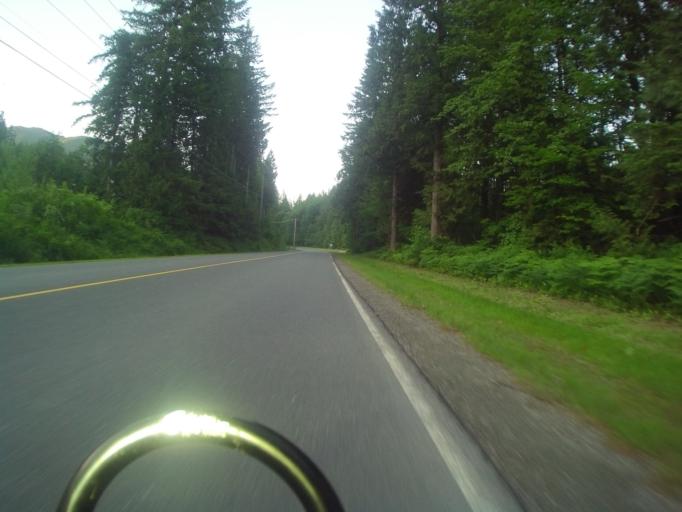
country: CA
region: British Columbia
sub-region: Fraser Valley Regional District
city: Chilliwack
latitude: 49.2940
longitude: -121.9422
